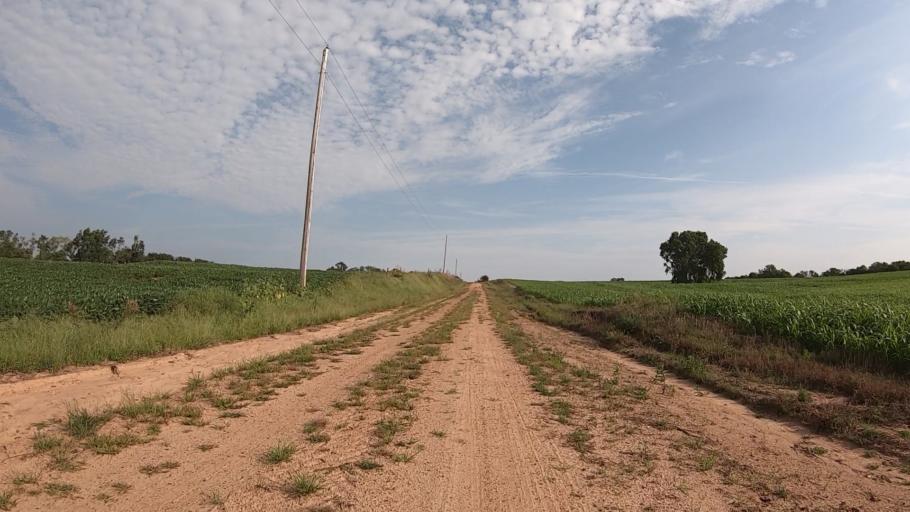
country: US
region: Kansas
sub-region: Washington County
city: Washington
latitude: 39.6728
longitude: -96.9471
